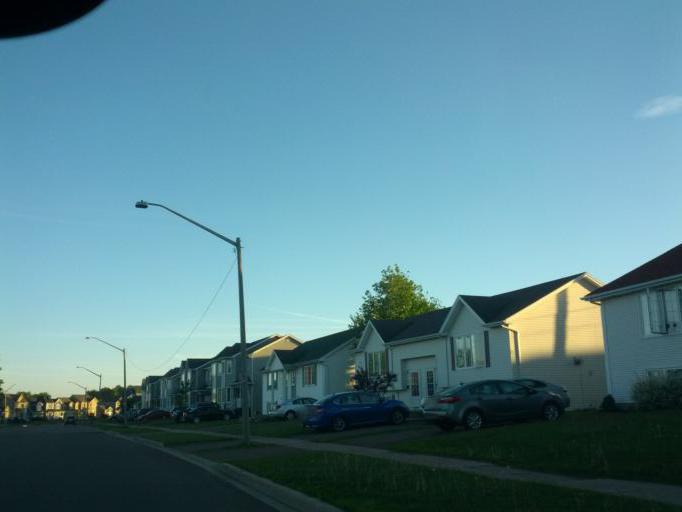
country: CA
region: New Brunswick
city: Moncton
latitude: 46.1138
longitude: -64.8619
